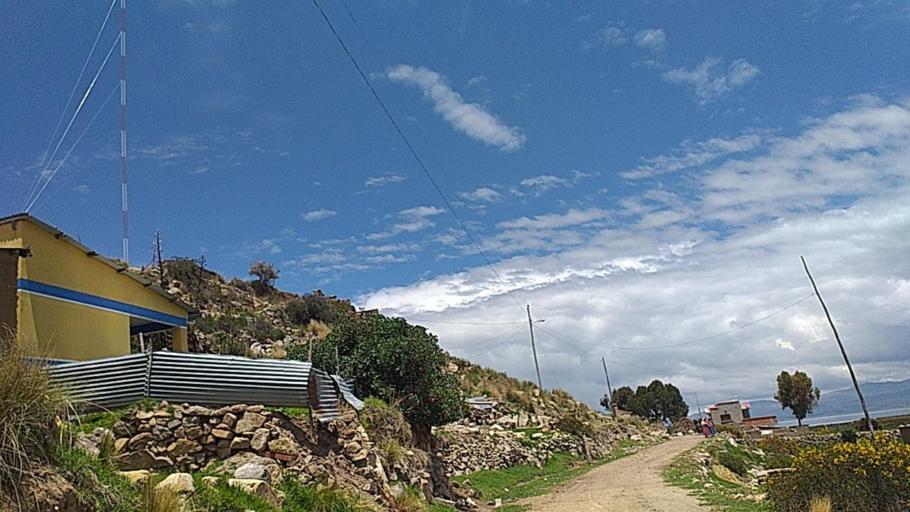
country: BO
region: La Paz
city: Huatajata
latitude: -16.3113
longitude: -68.6787
